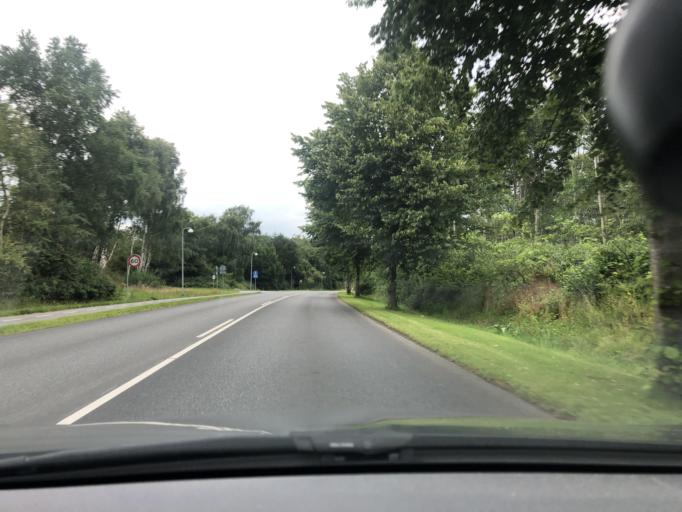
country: DK
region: South Denmark
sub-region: Vejle Kommune
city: Vejle
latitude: 55.6717
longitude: 9.5416
